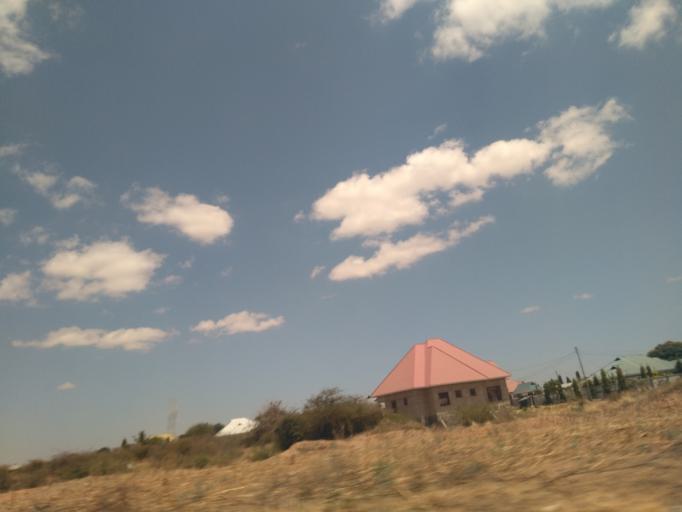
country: TZ
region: Dodoma
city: Kisasa
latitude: -6.1726
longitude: 35.7893
